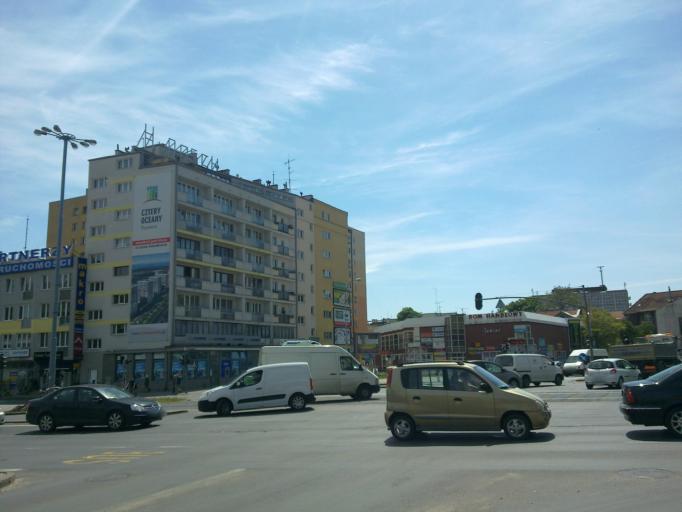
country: PL
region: Pomeranian Voivodeship
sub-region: Gdansk
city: Gdansk
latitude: 54.3761
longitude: 18.6145
